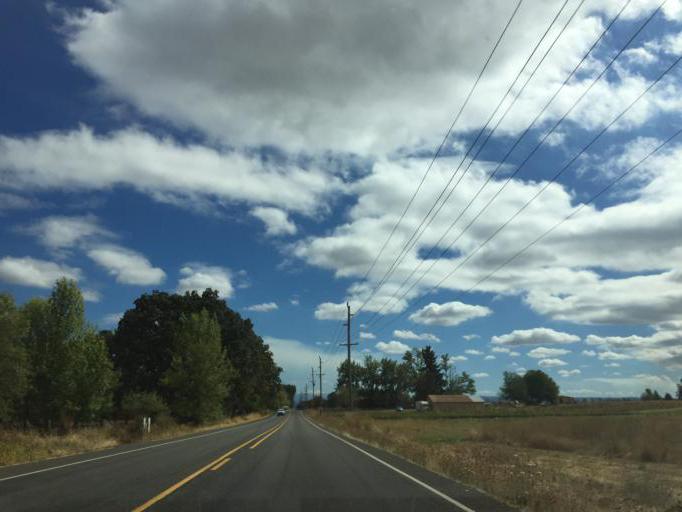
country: US
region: Oregon
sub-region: Marion County
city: Mount Angel
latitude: 45.1168
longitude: -122.7953
